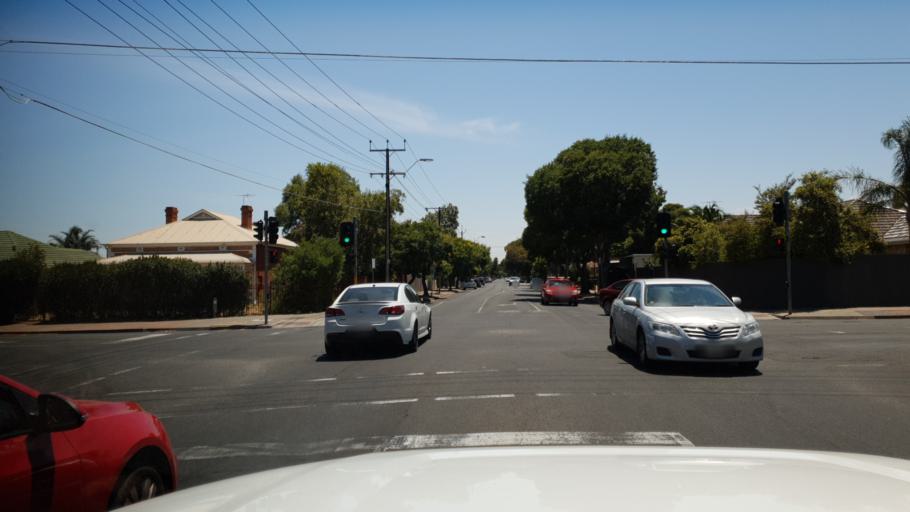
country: AU
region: South Australia
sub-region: Mitcham
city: Clarence Gardens
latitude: -34.9779
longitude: 138.5826
